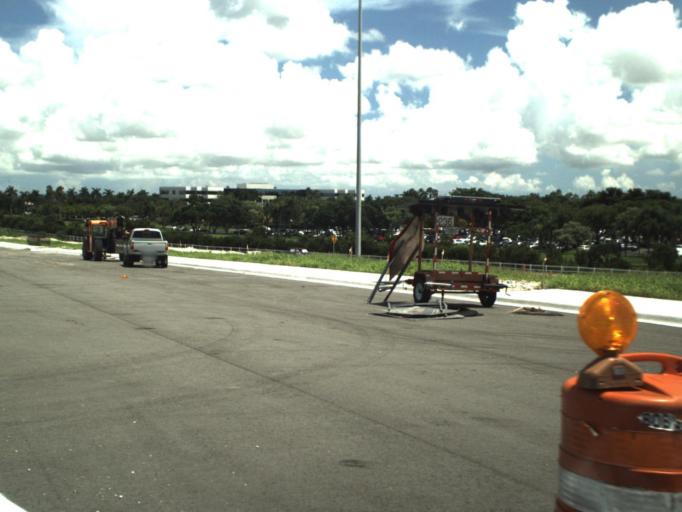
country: US
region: Florida
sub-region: Miami-Dade County
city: Country Club
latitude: 25.9784
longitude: -80.3501
